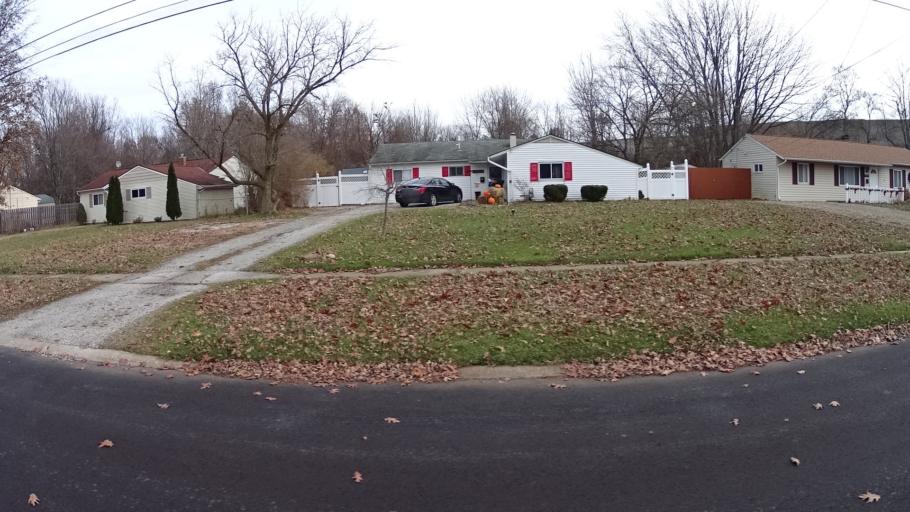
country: US
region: Ohio
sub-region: Lorain County
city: North Ridgeville
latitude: 41.3826
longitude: -81.9916
